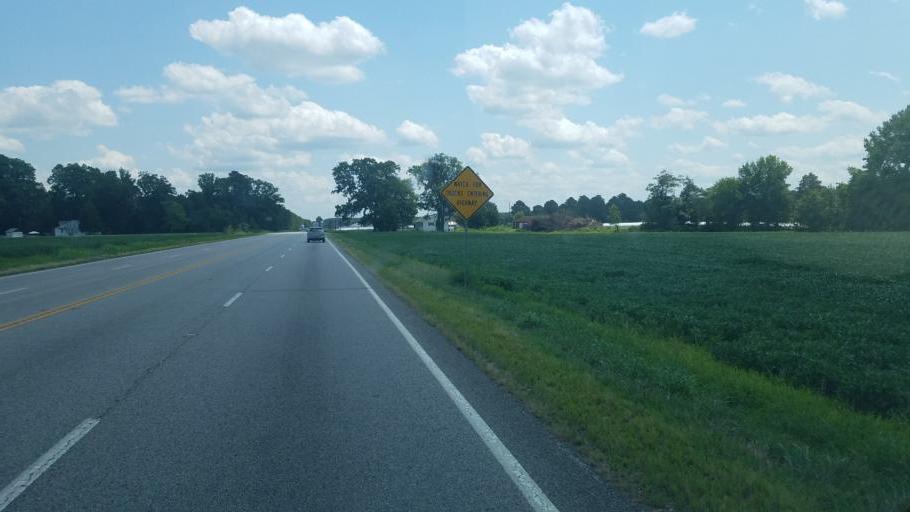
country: US
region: Virginia
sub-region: Sussex County
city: Waverly
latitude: 37.0824
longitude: -77.1593
